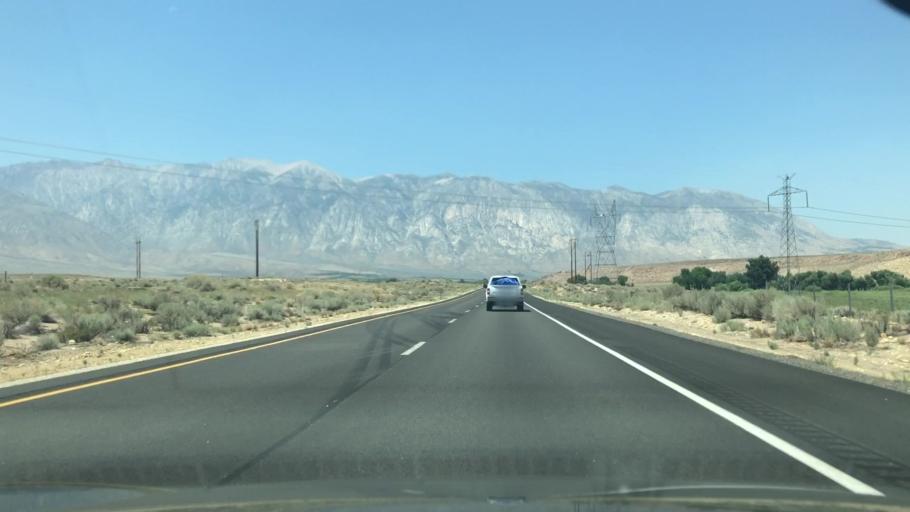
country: US
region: California
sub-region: Inyo County
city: West Bishop
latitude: 37.3942
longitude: -118.5124
